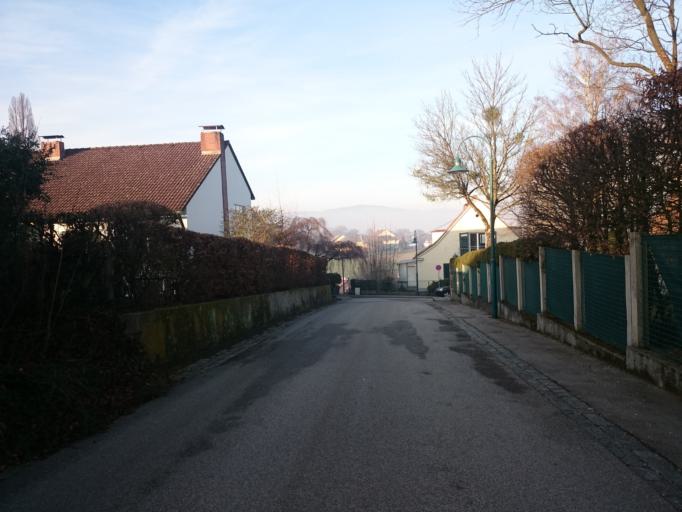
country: AT
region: Upper Austria
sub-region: Linz Stadt
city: Linz
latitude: 48.2967
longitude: 14.2786
